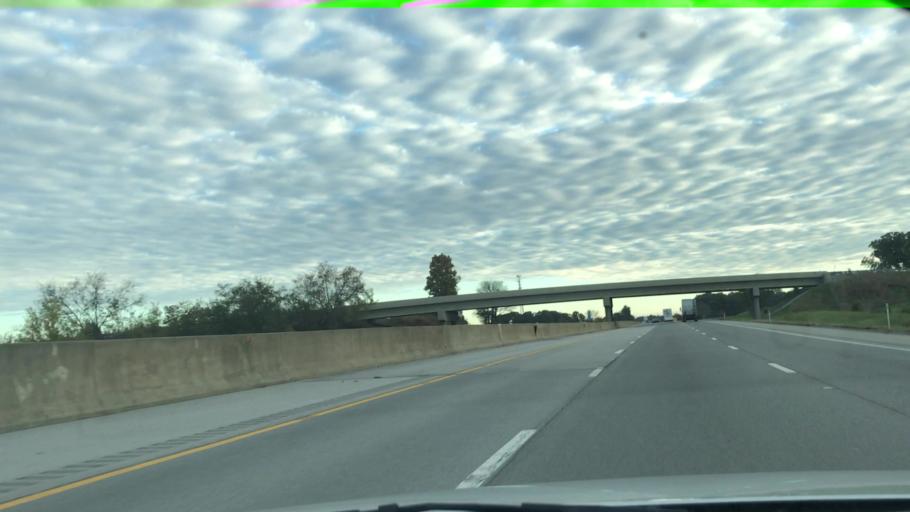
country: US
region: Kentucky
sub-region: Simpson County
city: Franklin
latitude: 36.7351
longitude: -86.5096
